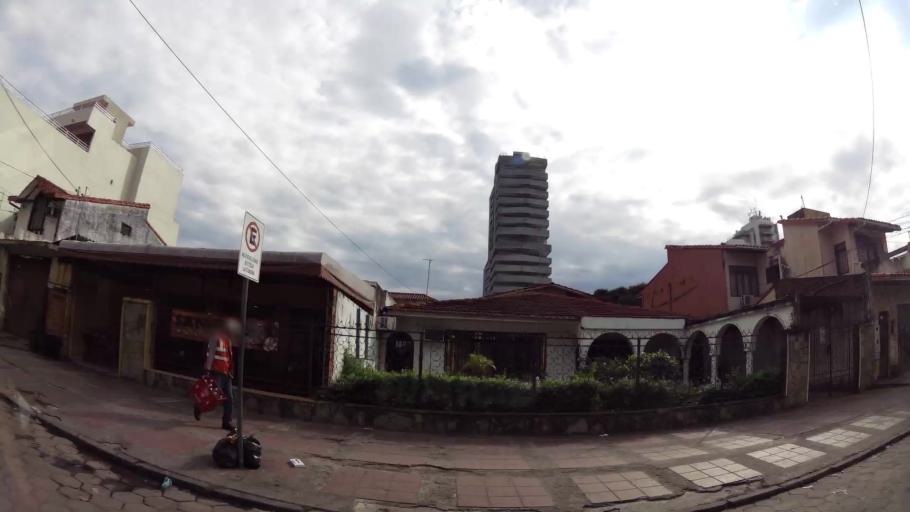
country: BO
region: Santa Cruz
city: Santa Cruz de la Sierra
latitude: -17.7950
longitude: -63.1761
